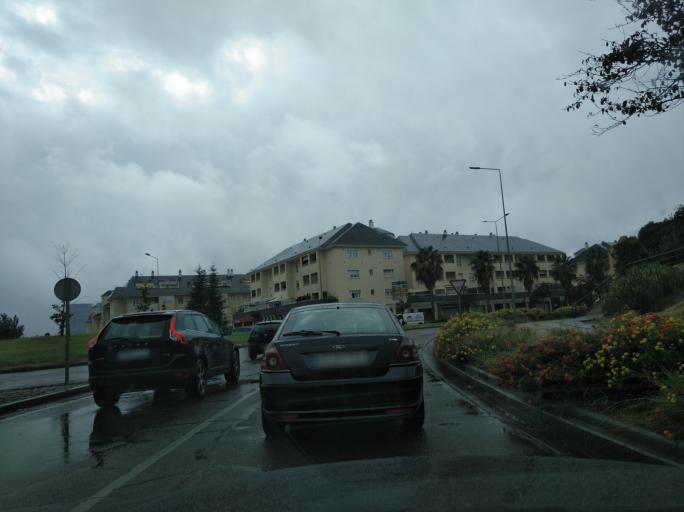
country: ES
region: Extremadura
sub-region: Provincia de Badajoz
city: Badajoz
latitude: 38.8838
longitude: -6.9913
